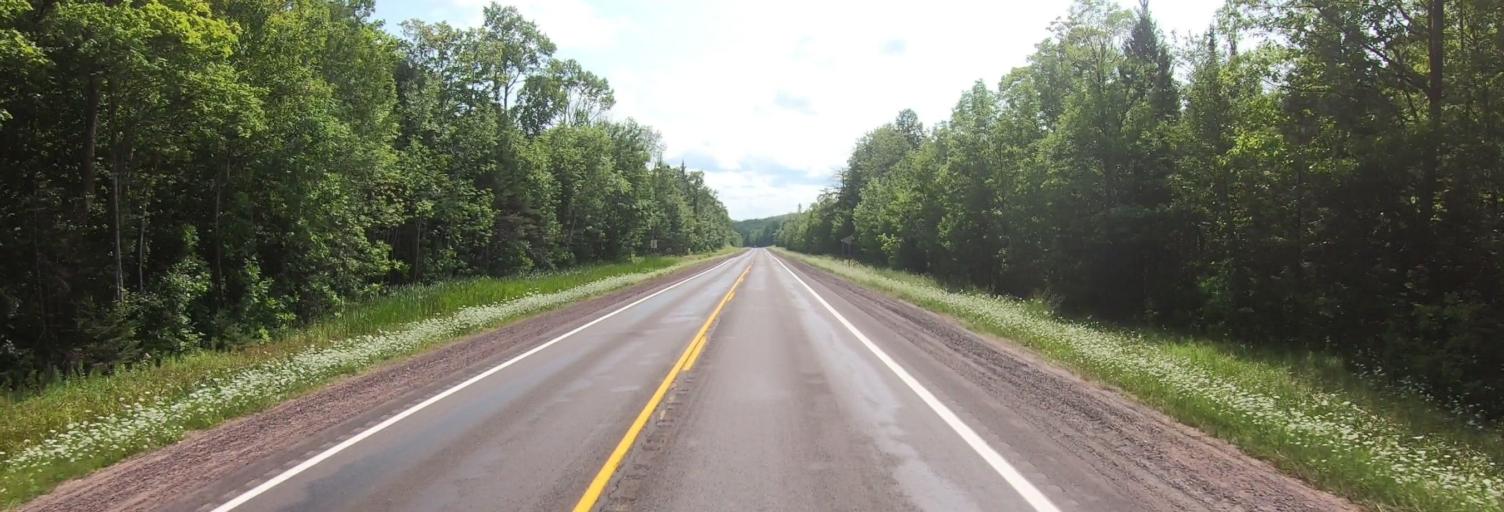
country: US
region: Michigan
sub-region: Ontonagon County
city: Ontonagon
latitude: 46.8426
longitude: -88.9864
